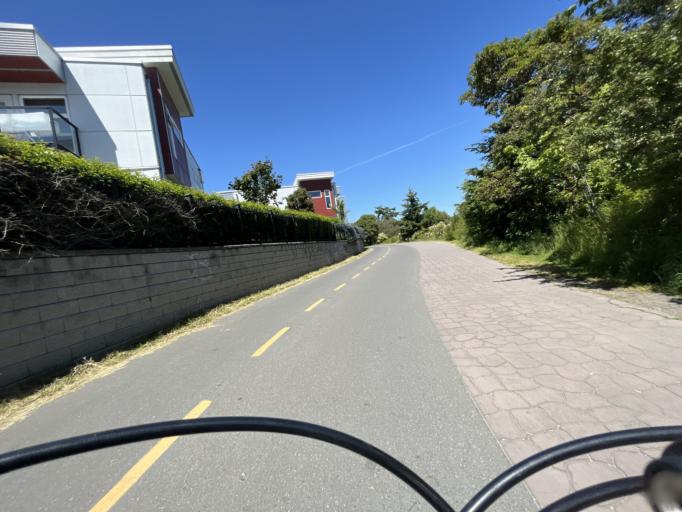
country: CA
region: British Columbia
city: Victoria
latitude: 48.4348
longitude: -123.3800
